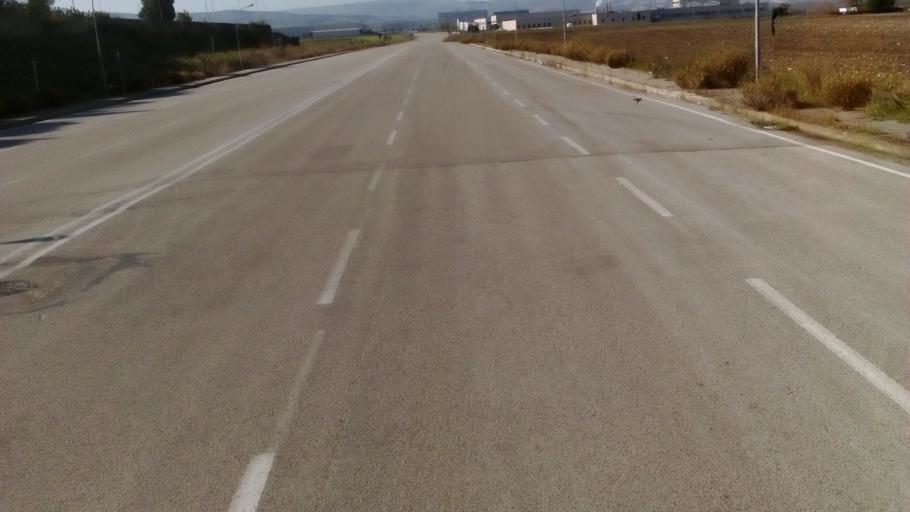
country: IT
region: Basilicate
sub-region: Provincia di Potenza
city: Melfi
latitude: 41.0778
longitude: 15.6715
